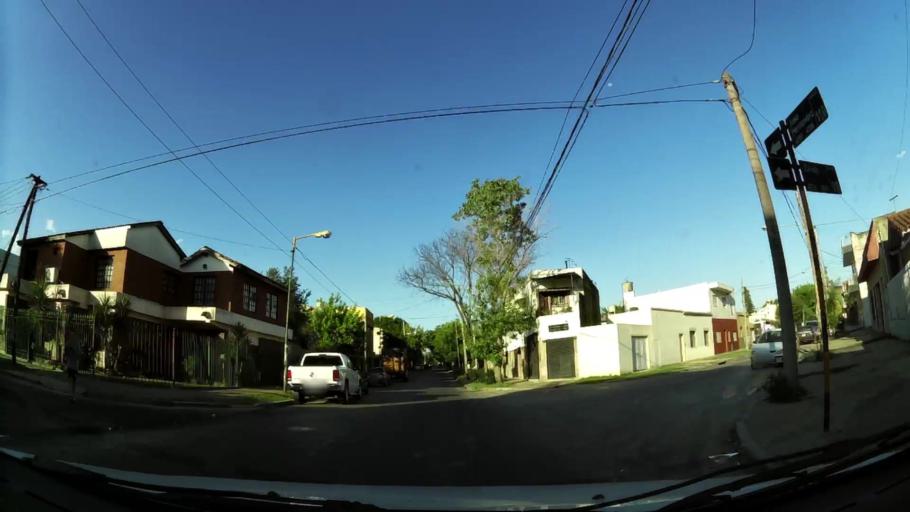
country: AR
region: Buenos Aires
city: Caseros
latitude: -34.5613
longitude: -58.5642
